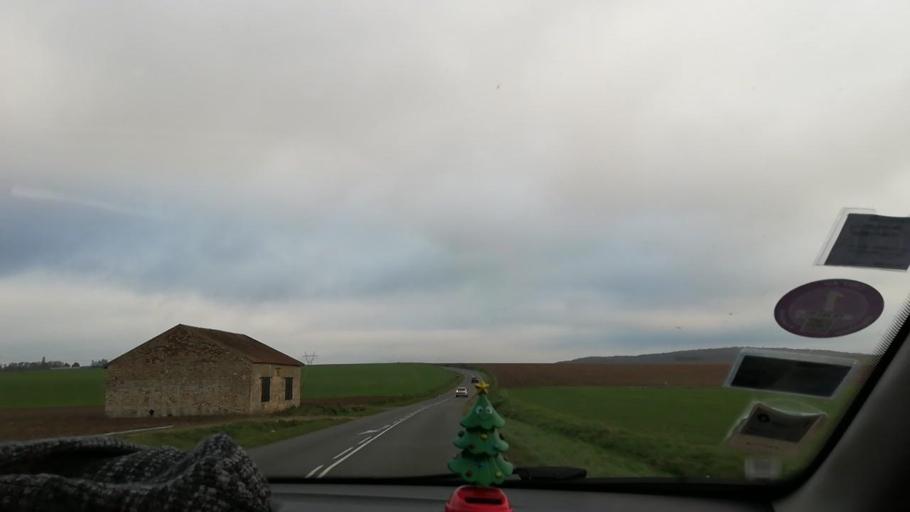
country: FR
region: Ile-de-France
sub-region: Departement de Seine-et-Marne
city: Monthyon
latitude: 48.9996
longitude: 2.8145
